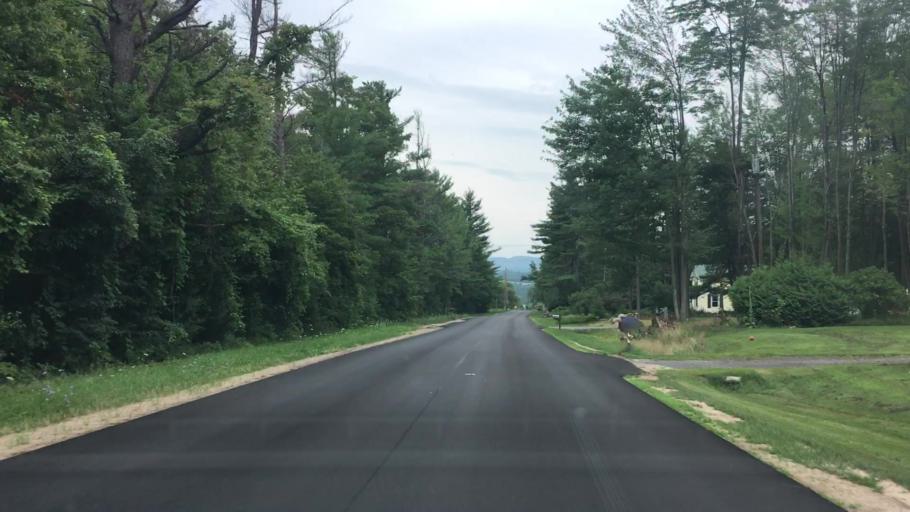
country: US
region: New York
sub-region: Clinton County
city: Peru
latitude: 44.5503
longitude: -73.5648
